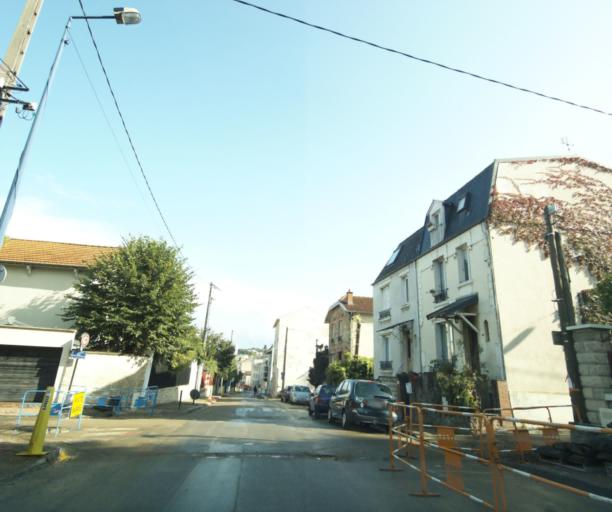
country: FR
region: Ile-de-France
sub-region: Departement des Hauts-de-Seine
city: Clamart
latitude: 48.8053
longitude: 2.2633
